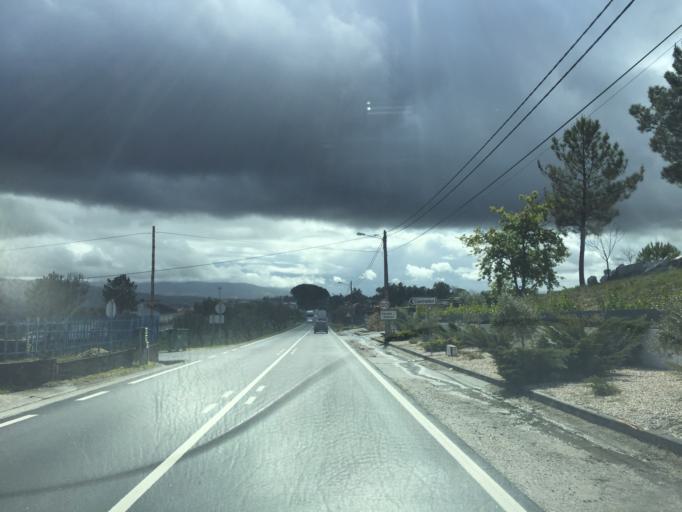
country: PT
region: Coimbra
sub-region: Oliveira do Hospital
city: Oliveira do Hospital
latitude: 40.3259
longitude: -7.8774
